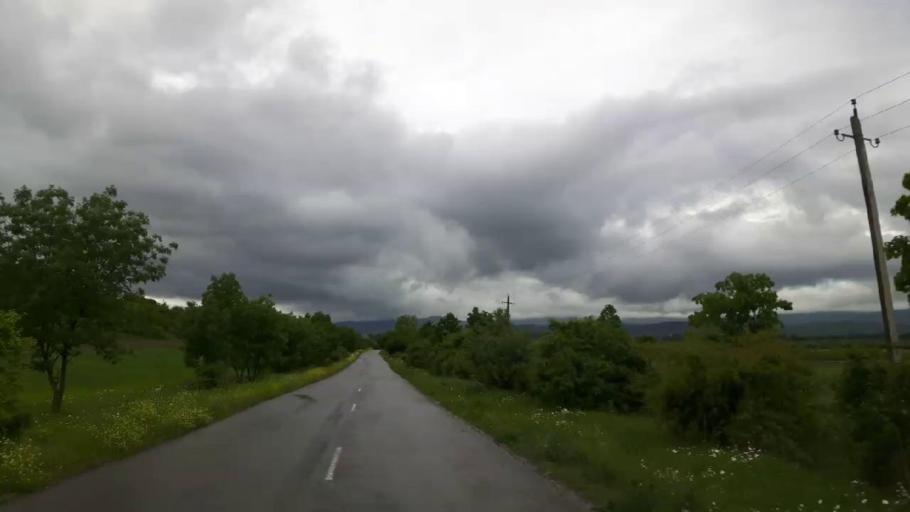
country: GE
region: Shida Kartli
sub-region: Khashuris Raioni
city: Khashuri
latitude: 41.9857
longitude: 43.6806
